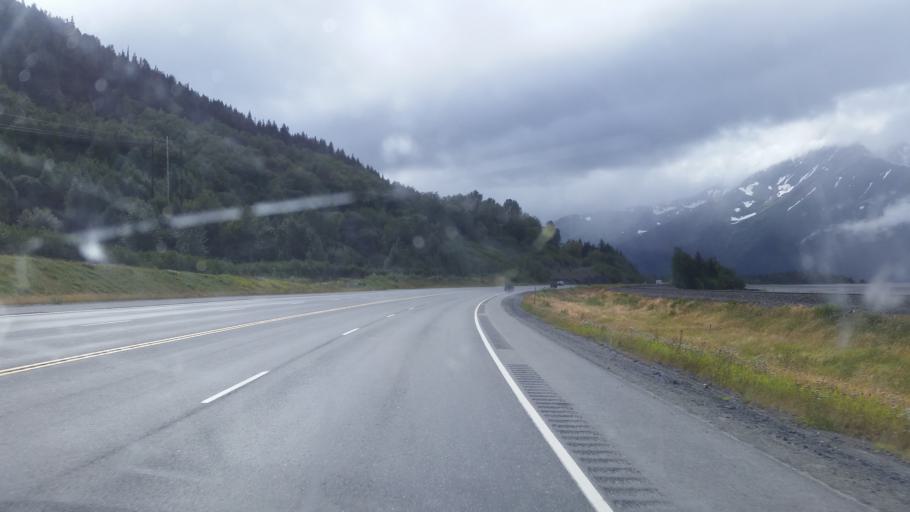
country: US
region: Alaska
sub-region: Anchorage Municipality
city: Girdwood
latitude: 60.9450
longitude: -149.3752
